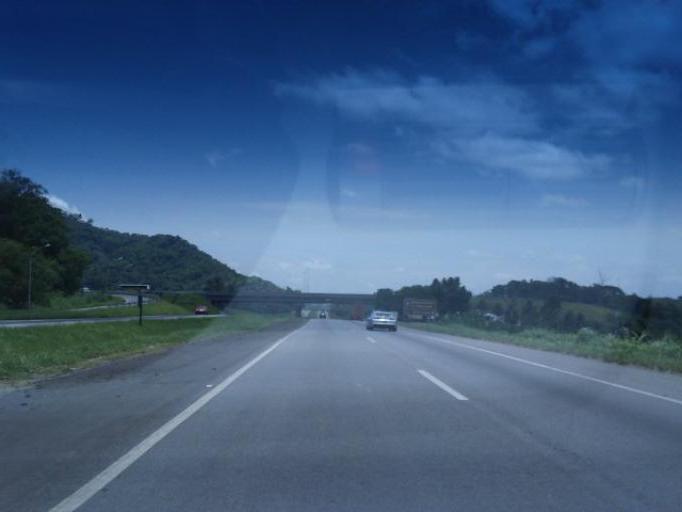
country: BR
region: Sao Paulo
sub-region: Miracatu
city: Miracatu
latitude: -24.3125
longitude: -47.5160
